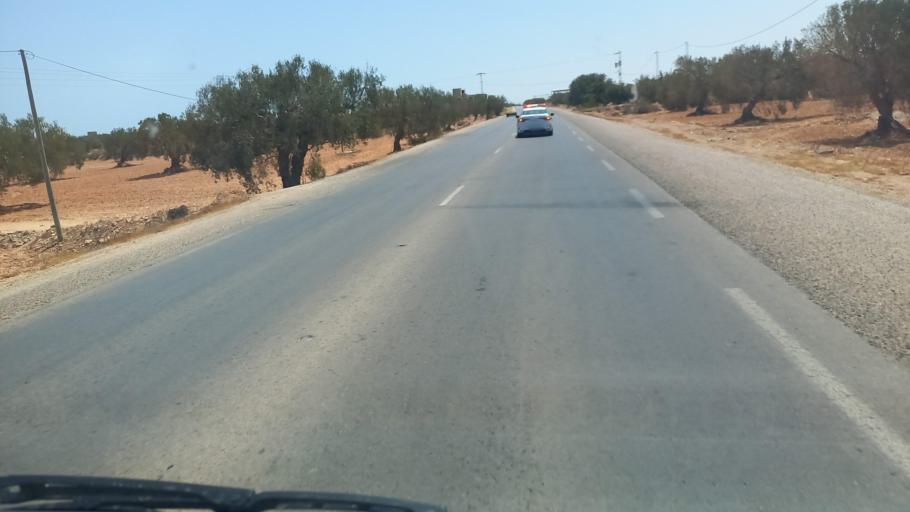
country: TN
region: Madanin
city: Zarzis
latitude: 33.5514
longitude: 11.0656
